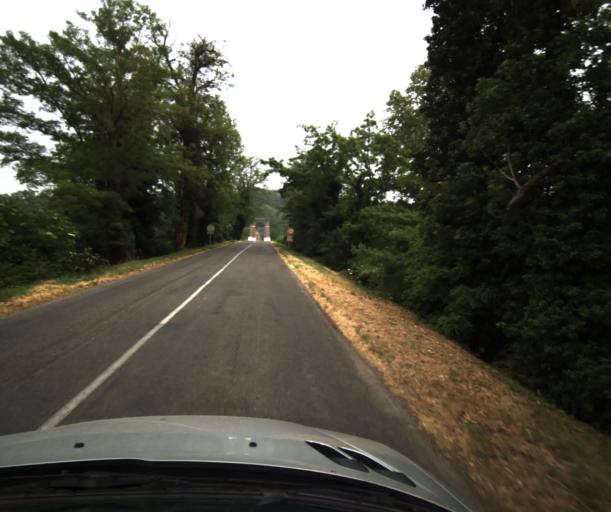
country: FR
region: Midi-Pyrenees
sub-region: Departement du Tarn-et-Garonne
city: Saint-Nicolas-de-la-Grave
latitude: 44.0901
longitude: 1.0279
